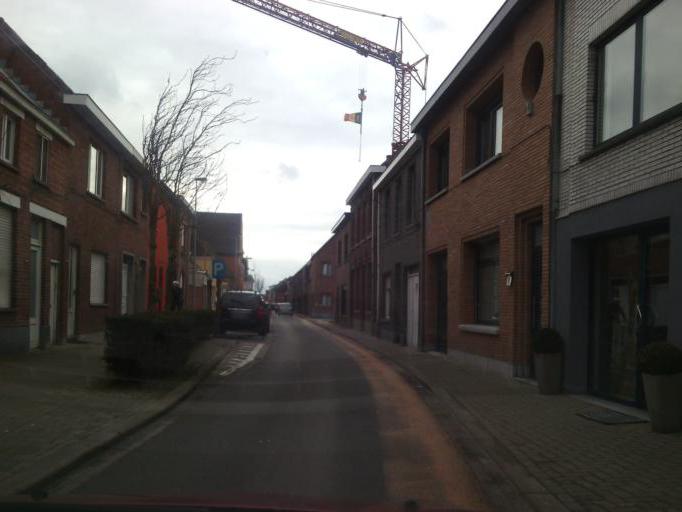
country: BE
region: Flanders
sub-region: Provincie Oost-Vlaanderen
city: Zele
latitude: 51.0649
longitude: 4.0228
